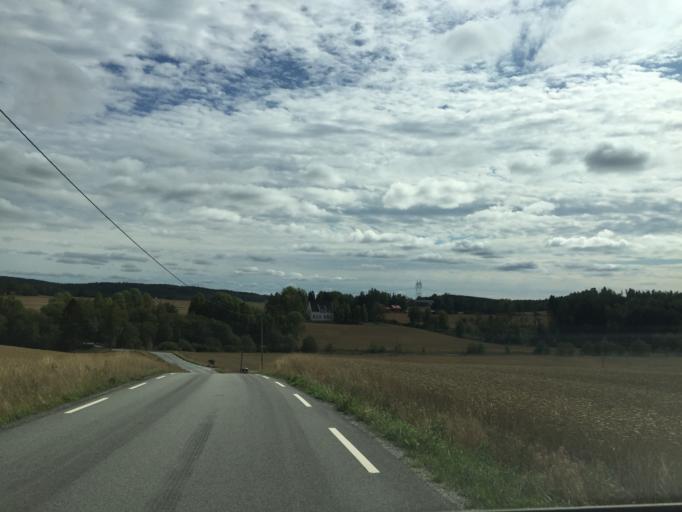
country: NO
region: Ostfold
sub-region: Hobol
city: Elvestad
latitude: 59.6489
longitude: 10.8807
